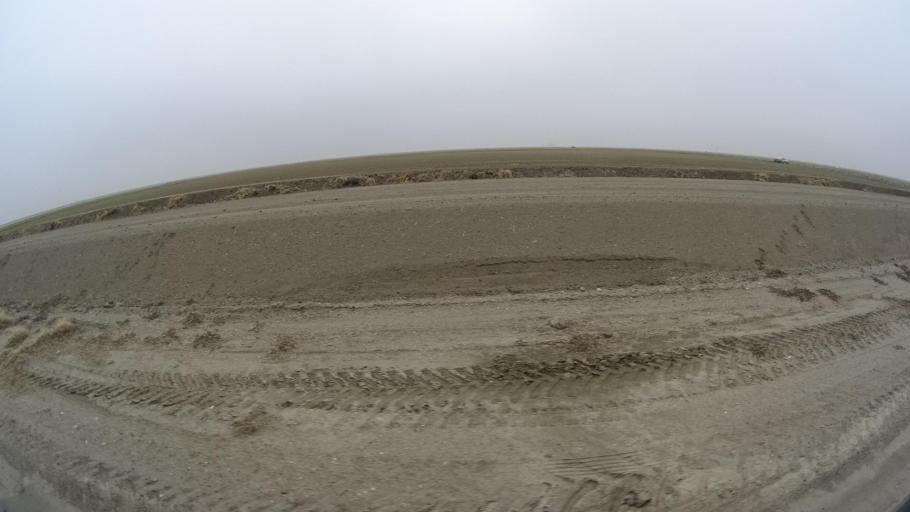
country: US
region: California
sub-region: Kern County
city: Rosedale
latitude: 35.1896
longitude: -119.1992
